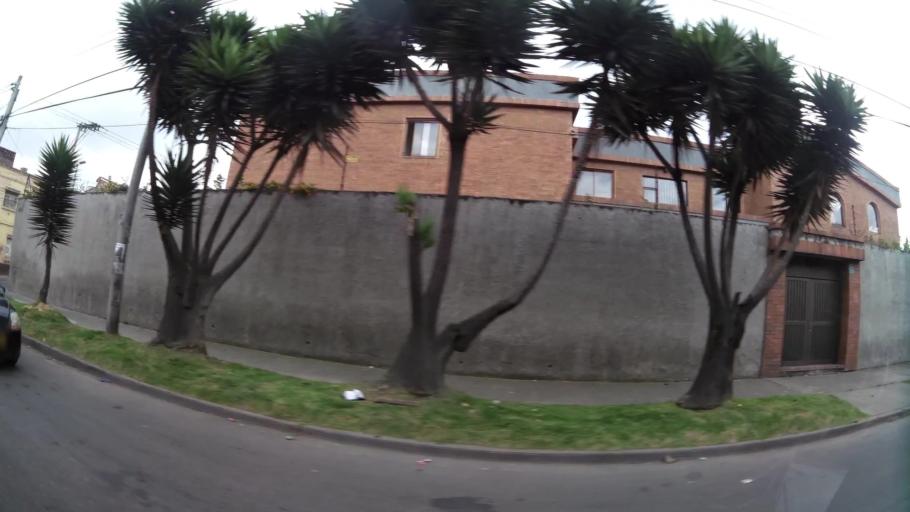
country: CO
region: Bogota D.C.
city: Bogota
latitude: 4.5828
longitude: -74.0864
